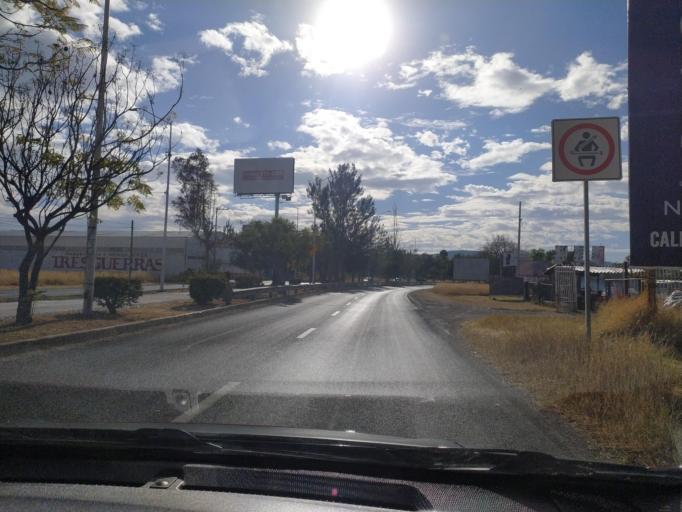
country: LA
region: Oudomxai
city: Muang La
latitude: 21.0317
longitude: 101.8313
